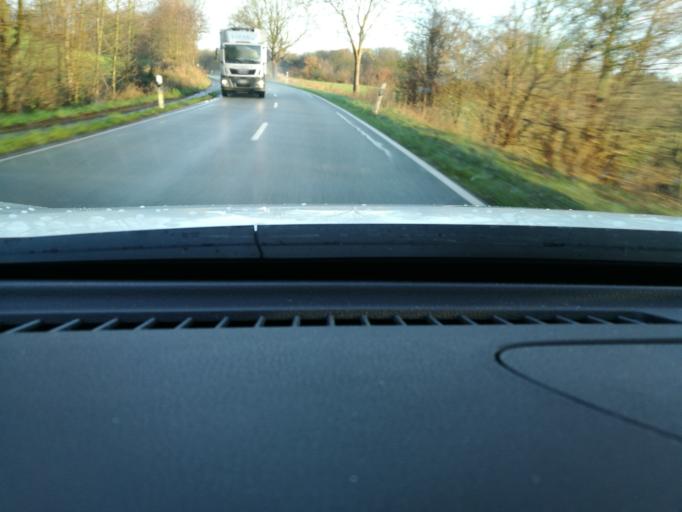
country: DE
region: Schleswig-Holstein
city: Ascheffel
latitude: 54.4151
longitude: 9.7028
